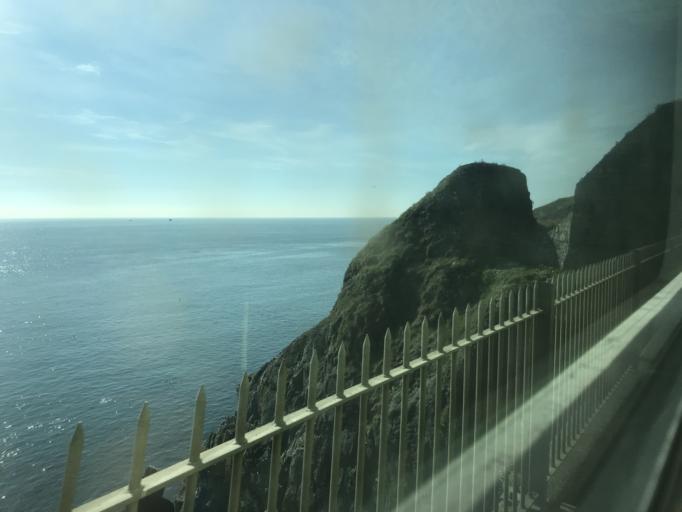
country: IE
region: Leinster
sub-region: Wicklow
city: Bray
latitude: 53.1803
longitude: -6.0754
